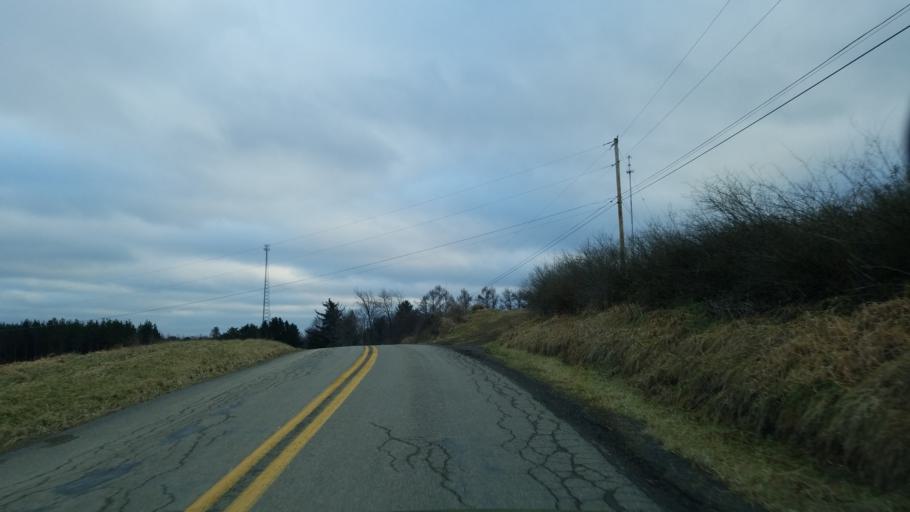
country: US
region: Pennsylvania
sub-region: Jefferson County
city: Falls Creek
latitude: 41.1713
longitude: -78.8127
